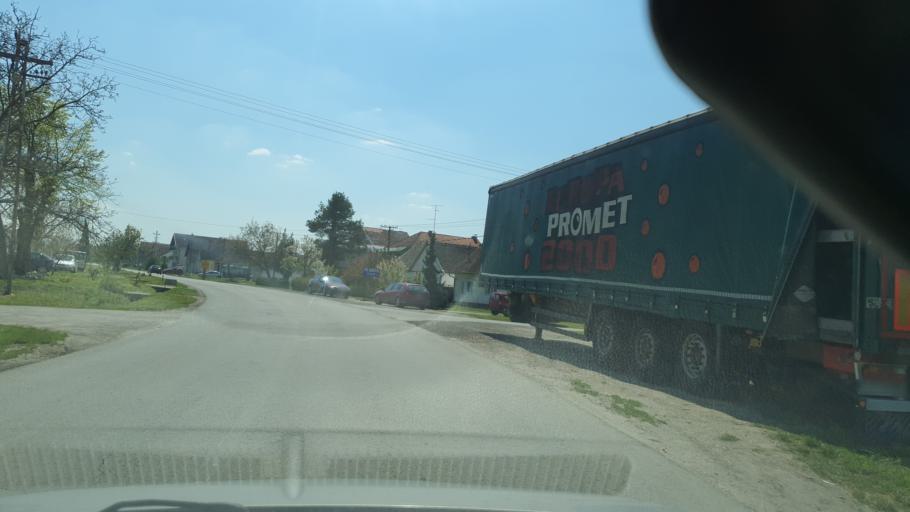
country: RS
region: Autonomna Pokrajina Vojvodina
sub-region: Juznobacki Okrug
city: Backa Palanka
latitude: 45.2575
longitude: 19.3976
